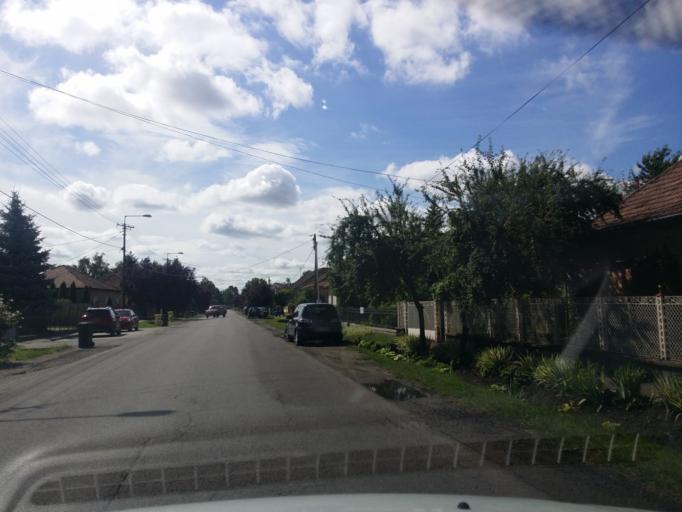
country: HU
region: Jasz-Nagykun-Szolnok
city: Jaszszentandras
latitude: 47.6500
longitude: 20.1567
